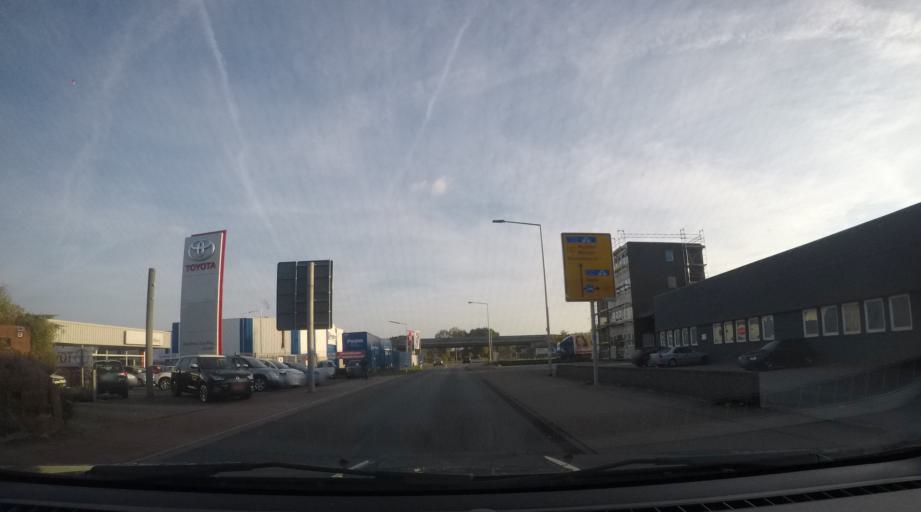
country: DE
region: North Rhine-Westphalia
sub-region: Regierungsbezirk Dusseldorf
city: Bocholt
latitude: 51.8249
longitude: 6.6304
